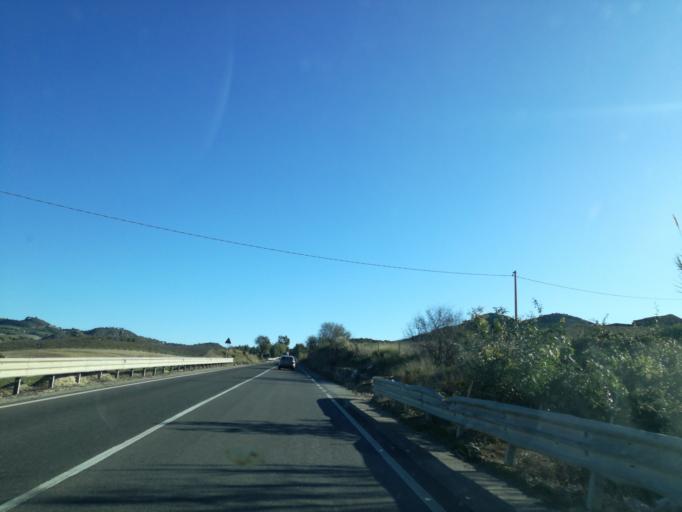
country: IT
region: Sicily
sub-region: Provincia di Caltanissetta
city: Niscemi
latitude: 37.2104
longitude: 14.3937
